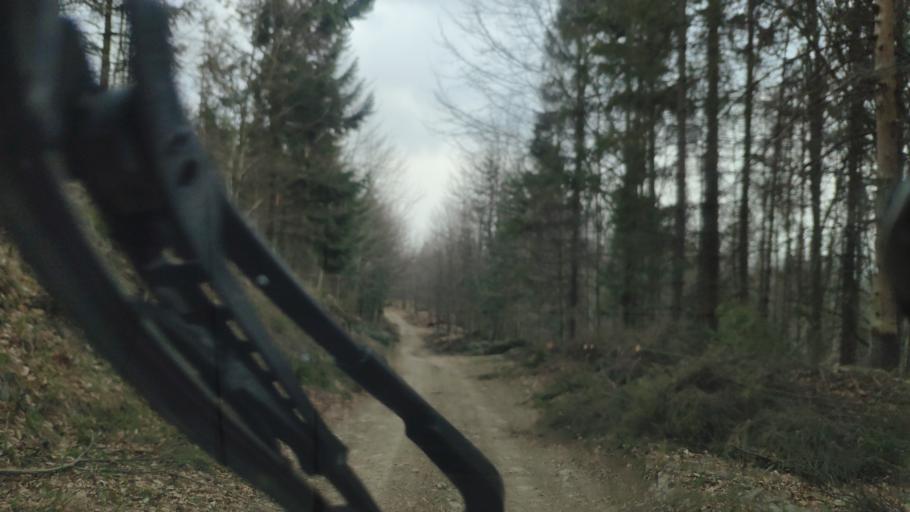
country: SK
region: Kosicky
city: Moldava nad Bodvou
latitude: 48.7467
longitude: 21.0405
